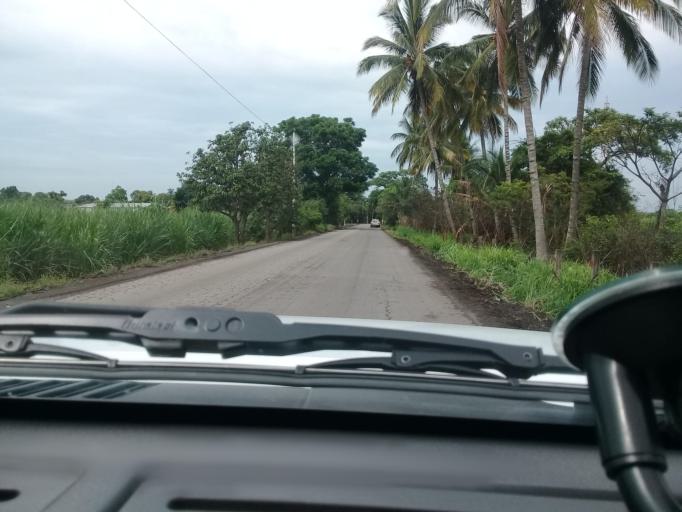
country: MX
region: Veracruz
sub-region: Paso de Ovejas
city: El Hatito
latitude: 19.3213
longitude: -96.3746
